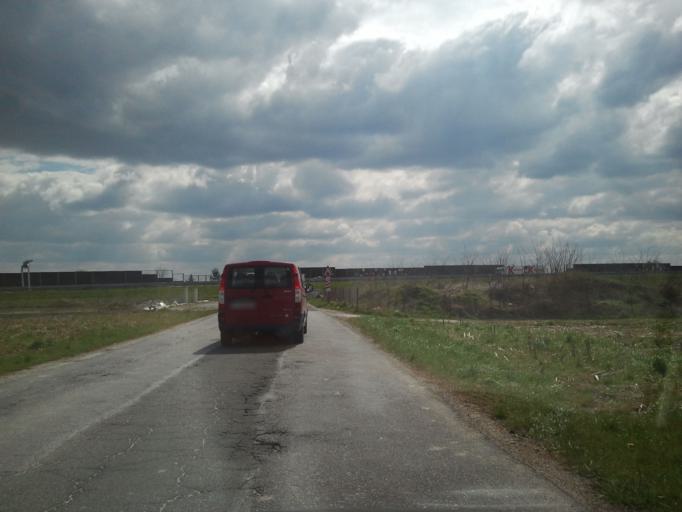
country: HR
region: Grad Zagreb
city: Brezovica
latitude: 45.7412
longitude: 15.8775
